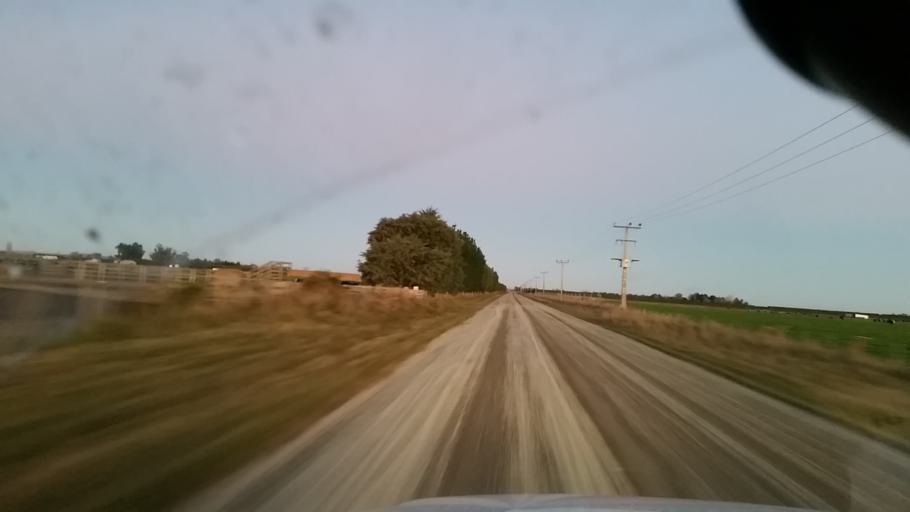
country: NZ
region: Canterbury
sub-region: Ashburton District
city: Tinwald
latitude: -43.9848
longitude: 171.6515
